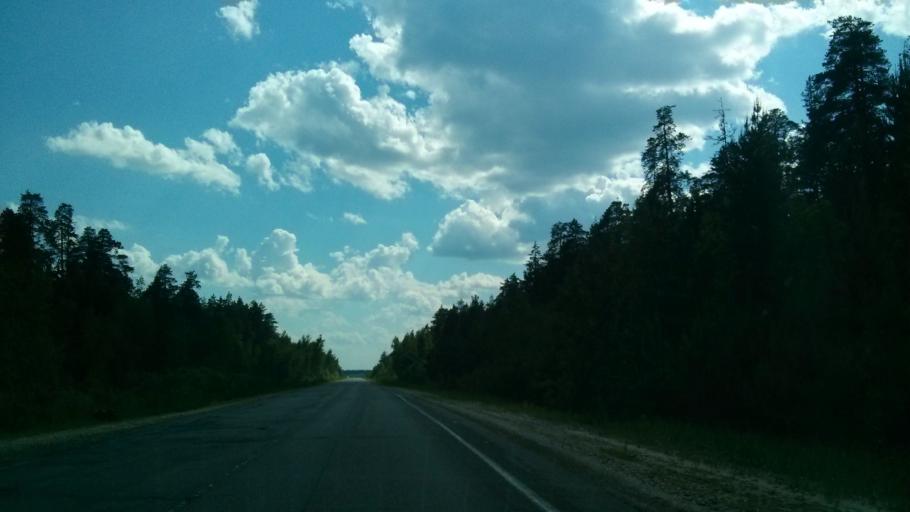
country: RU
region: Vladimir
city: Melenki
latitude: 55.3496
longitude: 41.6751
